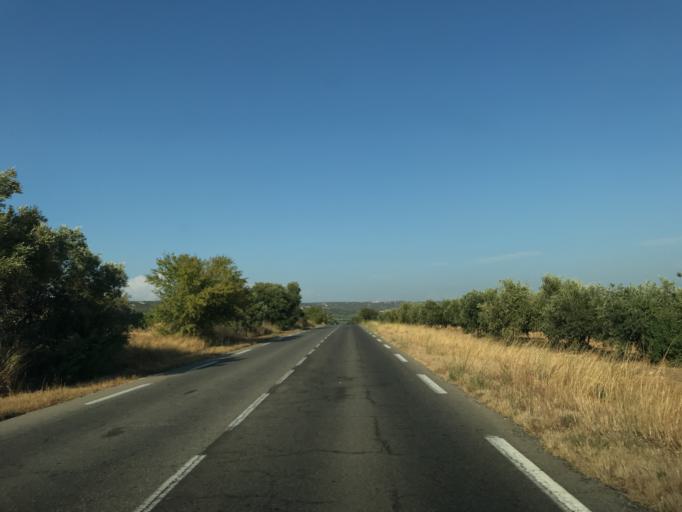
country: FR
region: Provence-Alpes-Cote d'Azur
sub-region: Departement des Bouches-du-Rhone
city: Lancon-Provence
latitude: 43.5411
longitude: 5.1283
